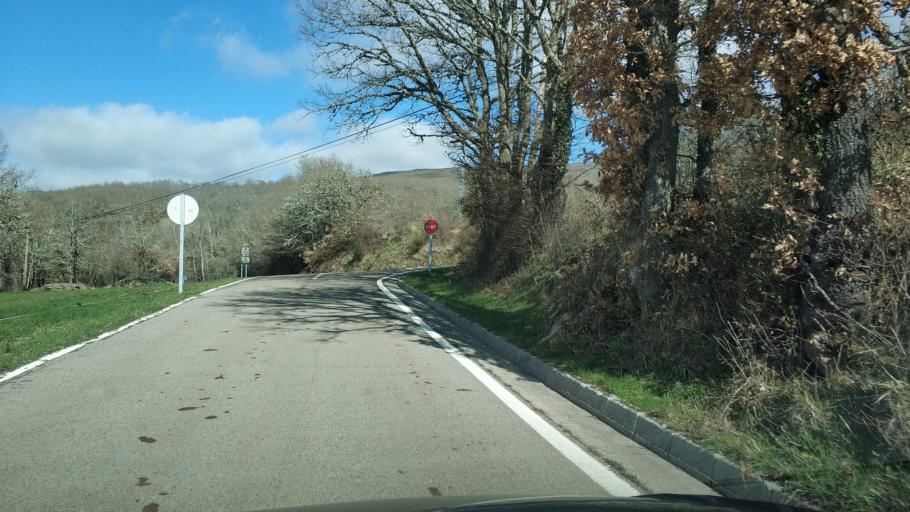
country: ES
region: Cantabria
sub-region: Provincia de Cantabria
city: Mataporquera
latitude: 42.9064
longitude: -4.0601
